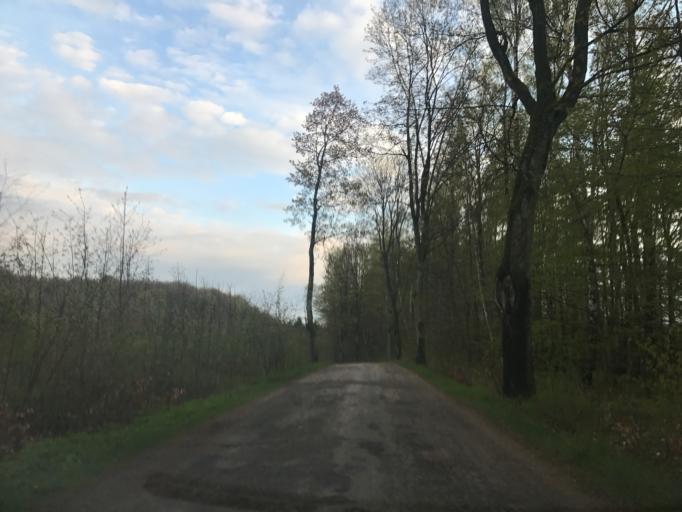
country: PL
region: Warmian-Masurian Voivodeship
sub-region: Powiat ilawski
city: Lubawa
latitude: 53.5539
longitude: 19.8968
